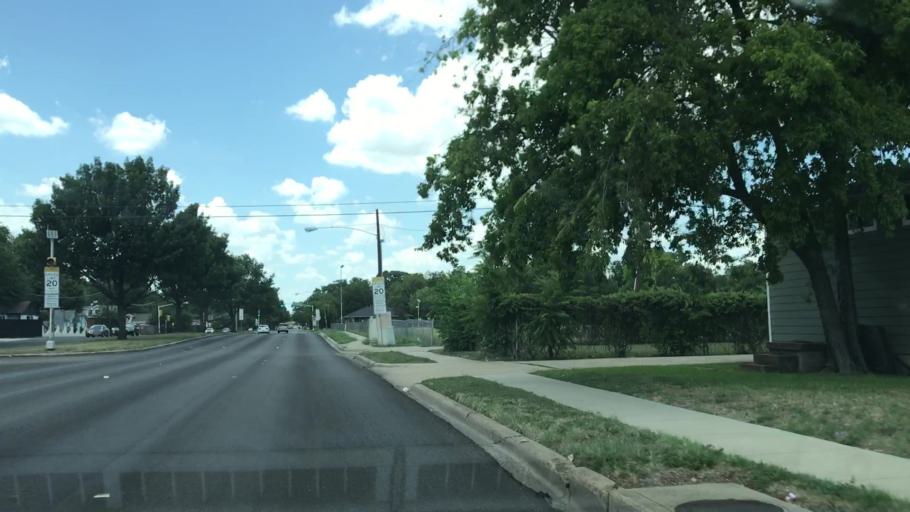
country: US
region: Texas
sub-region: Dallas County
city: University Park
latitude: 32.8691
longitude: -96.8560
